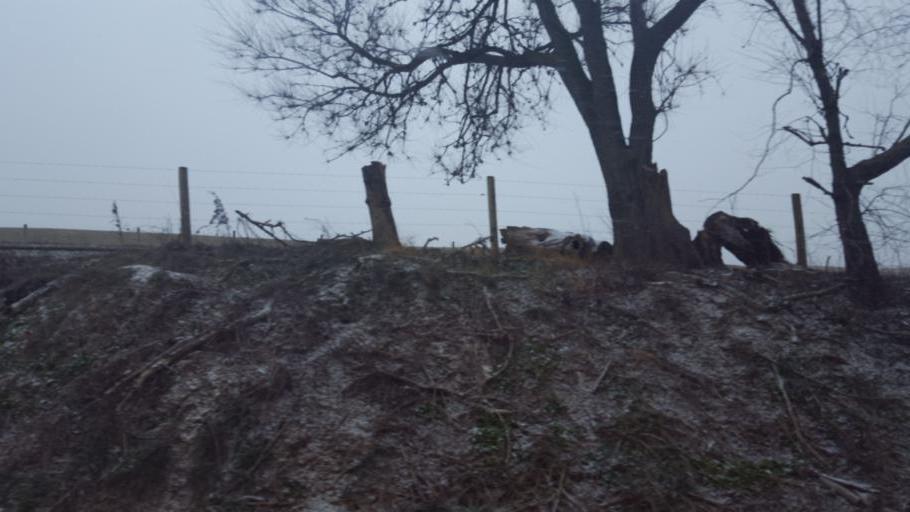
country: US
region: Ohio
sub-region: Tuscarawas County
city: Sugarcreek
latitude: 40.4777
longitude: -81.7322
